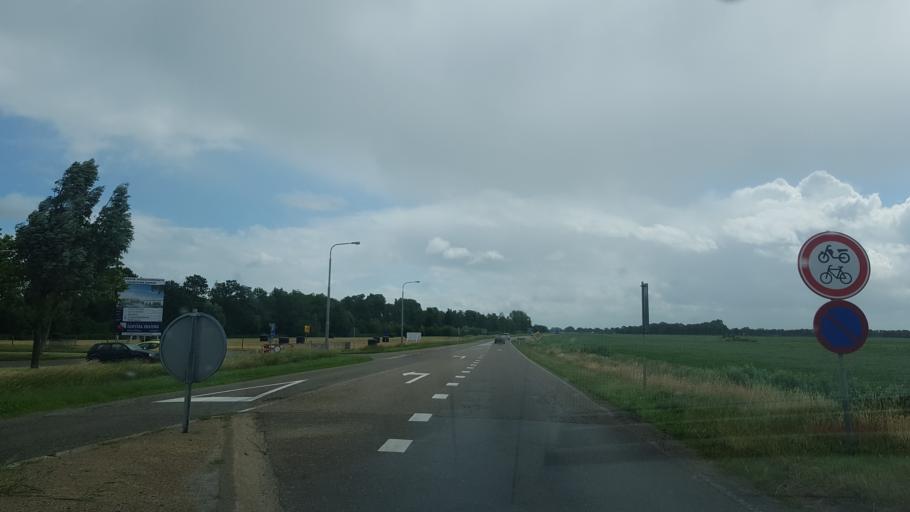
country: NL
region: Friesland
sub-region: Gemeente Dongeradeel
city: Dokkum
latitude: 53.3108
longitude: 5.9941
